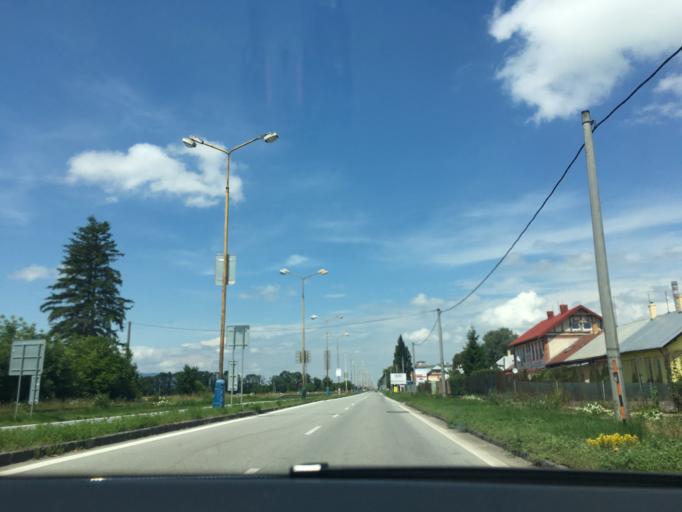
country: SK
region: Kosicky
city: Trebisov
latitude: 48.6398
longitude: 21.7163
